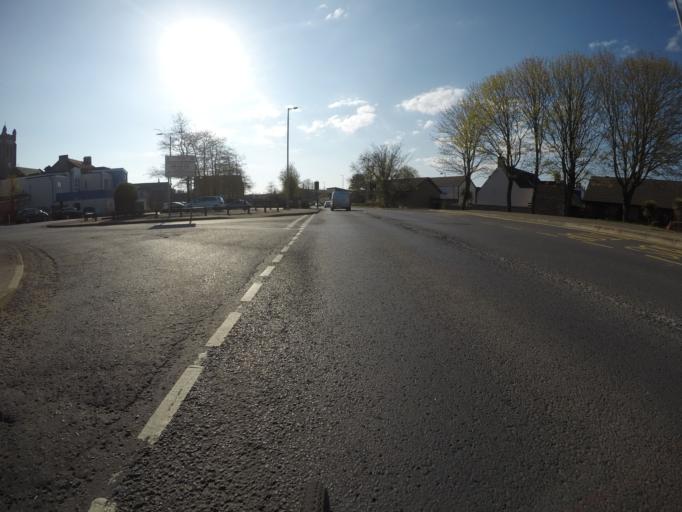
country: GB
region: Scotland
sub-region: North Ayrshire
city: Kilwinning
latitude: 55.6545
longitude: -4.6975
